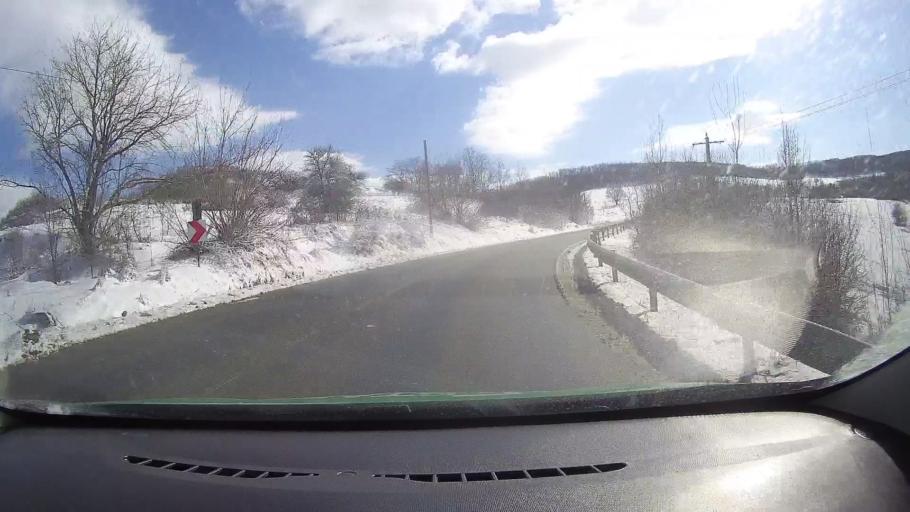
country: RO
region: Sibiu
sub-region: Comuna Barghis
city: Barghis
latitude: 45.9819
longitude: 24.5105
